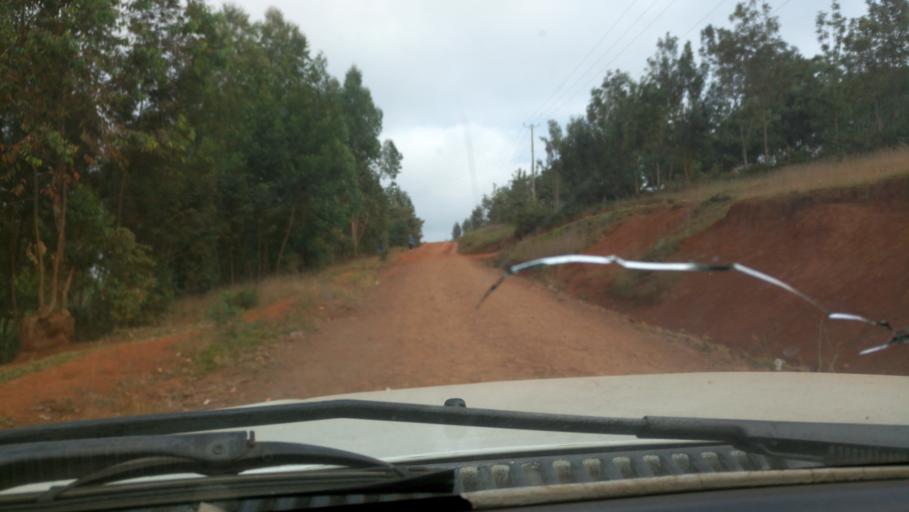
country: KE
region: Murang'a District
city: Maragua
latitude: -0.8409
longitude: 36.9967
